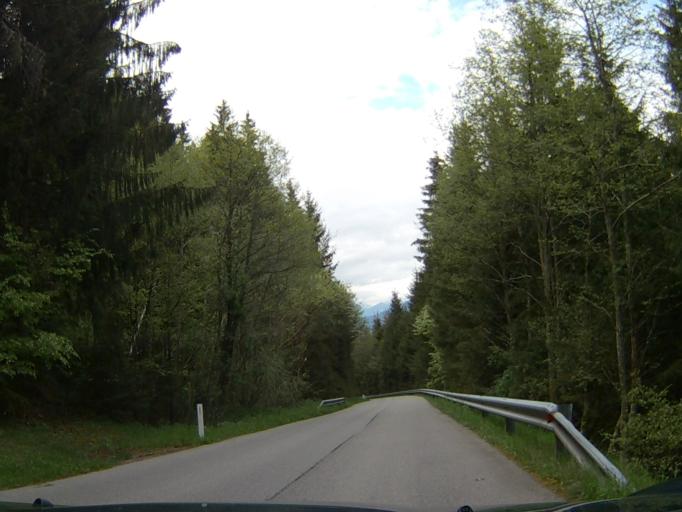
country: AT
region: Carinthia
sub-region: Politischer Bezirk Villach Land
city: Stockenboi
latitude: 46.7374
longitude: 13.5641
